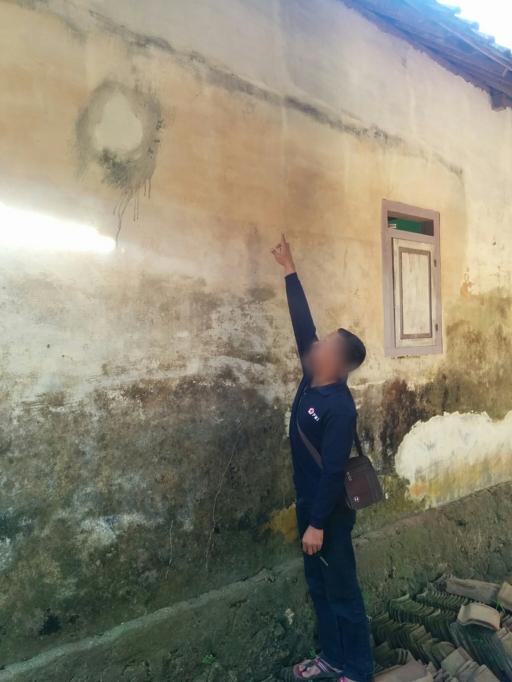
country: ID
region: East Java
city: Sitiarjo
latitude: -8.4015
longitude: 112.6598
